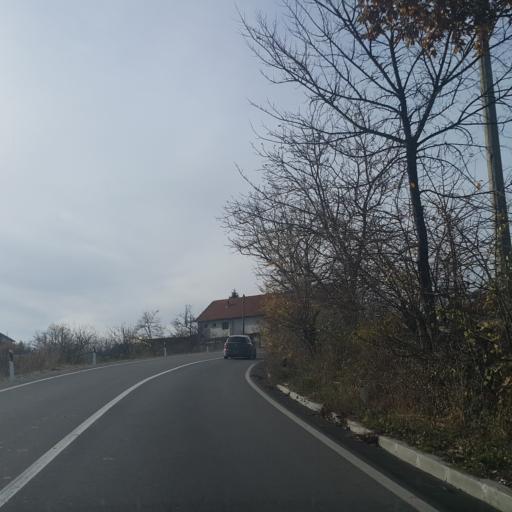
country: RS
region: Central Serbia
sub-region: Sumadijski Okrug
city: Arangelovac
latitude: 44.3341
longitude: 20.4333
